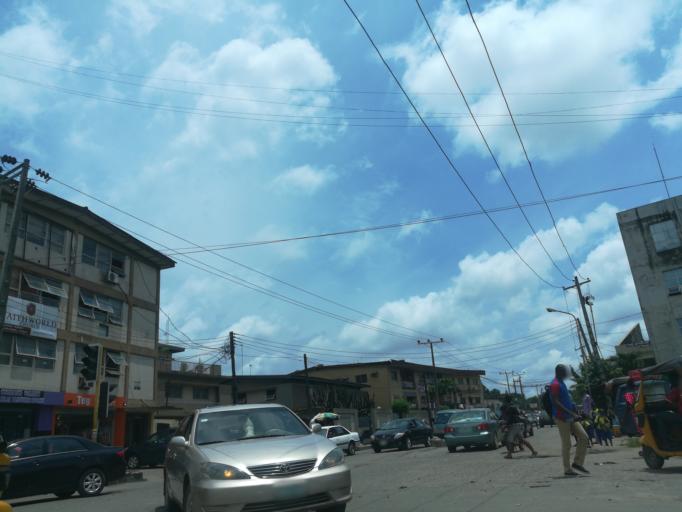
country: NG
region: Lagos
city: Somolu
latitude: 6.5466
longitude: 3.3620
